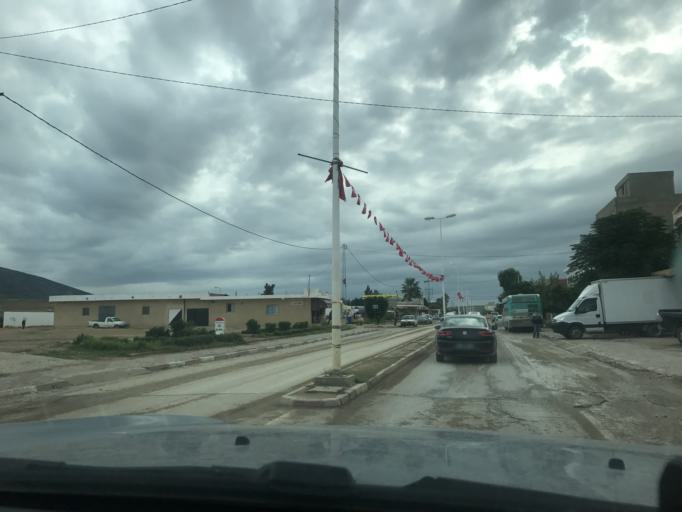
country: TN
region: Silyanah
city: Siliana
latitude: 36.0948
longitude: 9.5707
